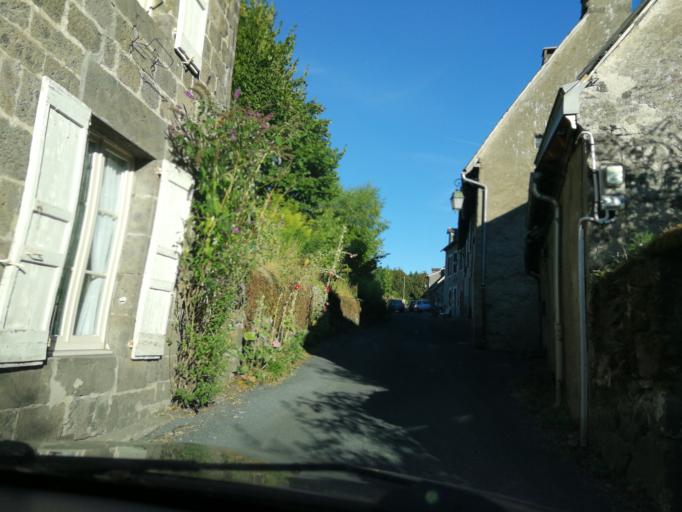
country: FR
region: Auvergne
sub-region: Departement du Cantal
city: Saint-Cernin
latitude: 45.1129
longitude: 2.5046
